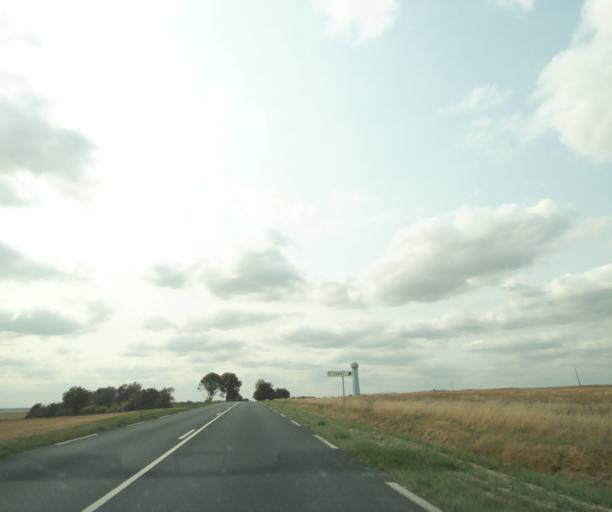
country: FR
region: Centre
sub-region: Departement de l'Indre
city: Buzancais
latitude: 46.9068
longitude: 1.3488
